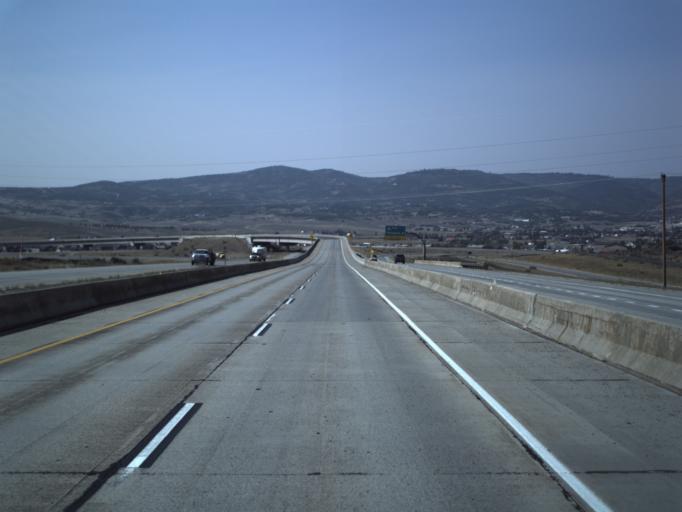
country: US
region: Utah
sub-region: Summit County
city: Snyderville
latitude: 40.7258
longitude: -111.4931
